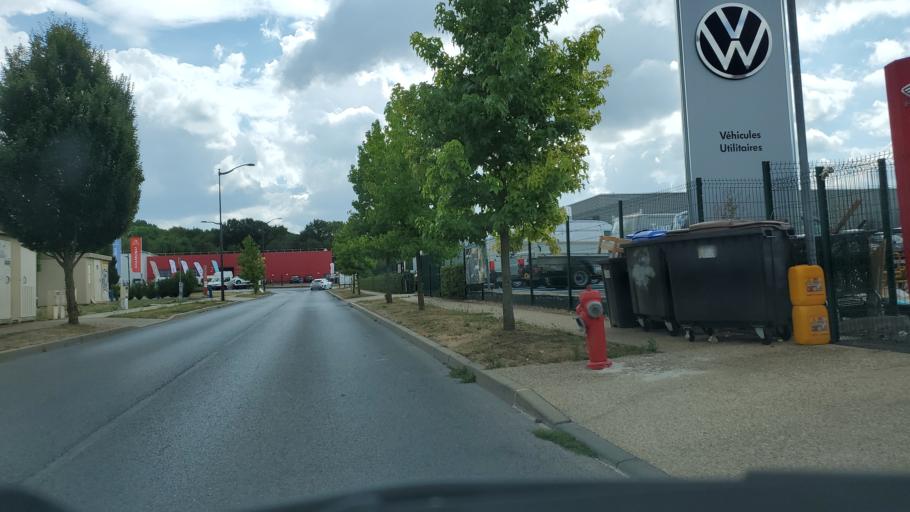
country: FR
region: Ile-de-France
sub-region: Departement de Seine-et-Marne
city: Mareuil-les-Meaux
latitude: 48.9343
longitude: 2.8770
